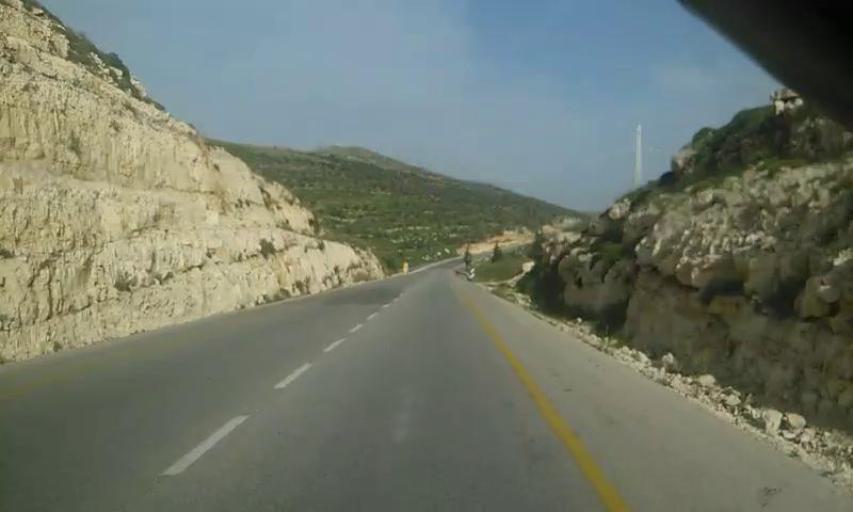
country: PS
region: West Bank
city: Till
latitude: 32.1912
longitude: 35.1995
